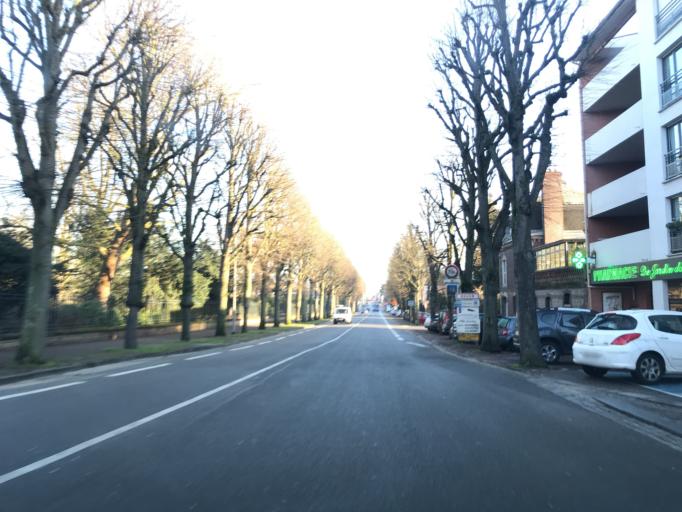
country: FR
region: Haute-Normandie
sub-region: Departement de la Seine-Maritime
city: Sotteville-les-Rouen
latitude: 49.4197
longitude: 1.0782
